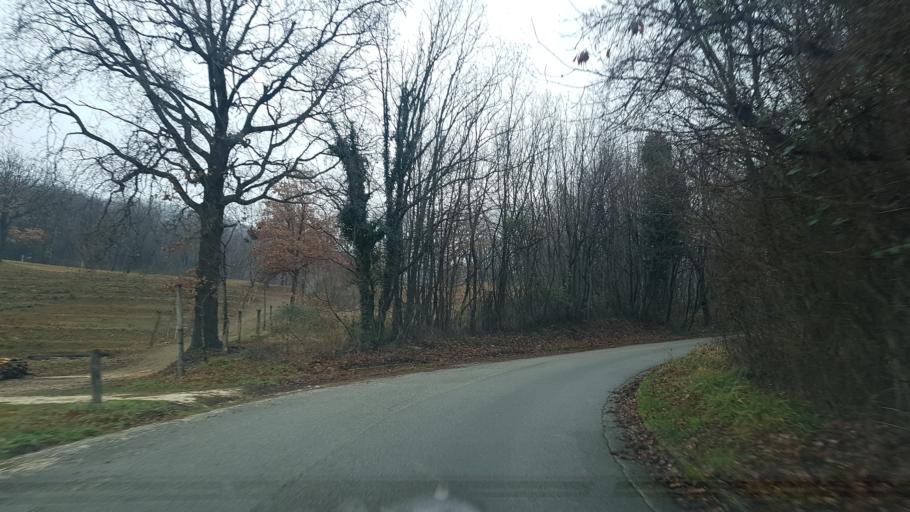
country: IT
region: Friuli Venezia Giulia
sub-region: Provincia di Udine
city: San Pietro al Natisone
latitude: 46.0841
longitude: 13.4829
